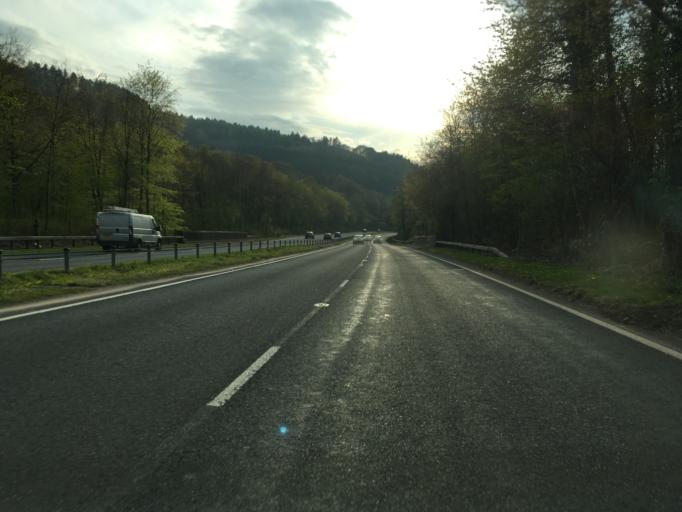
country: GB
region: Wales
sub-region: Caerphilly County Borough
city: Crosskeys
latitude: 51.6150
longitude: -3.1187
